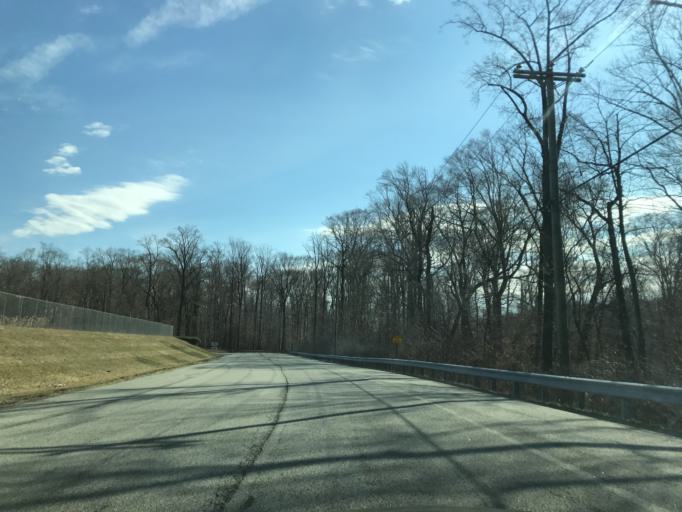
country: US
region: Maryland
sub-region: Cecil County
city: Perryville
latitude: 39.5577
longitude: -76.0618
